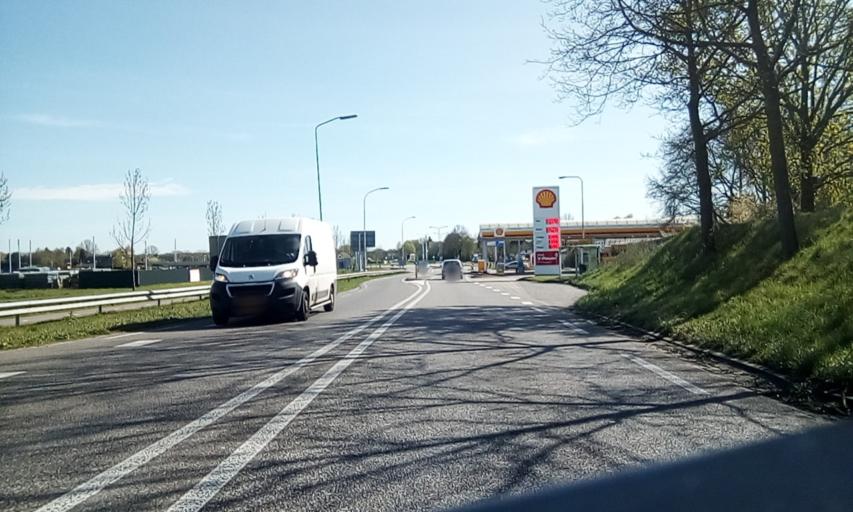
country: NL
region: Gelderland
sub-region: Gemeente Wijchen
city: Wijchen
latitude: 51.8243
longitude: 5.7376
